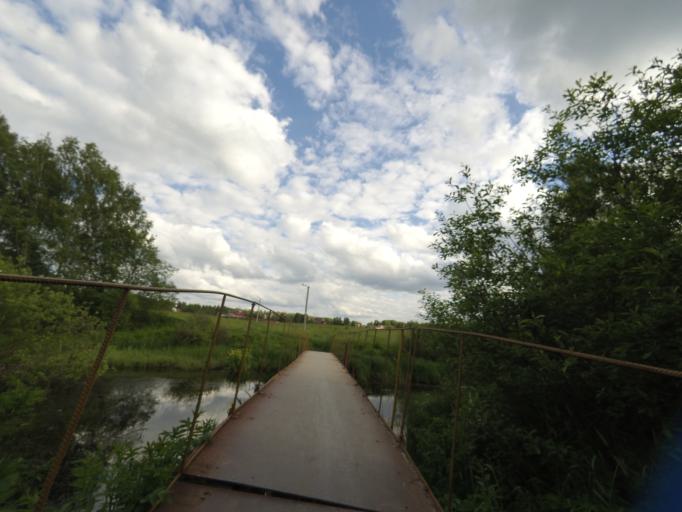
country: RU
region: Moskovskaya
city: Lugovaya
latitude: 56.0709
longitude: 37.4977
